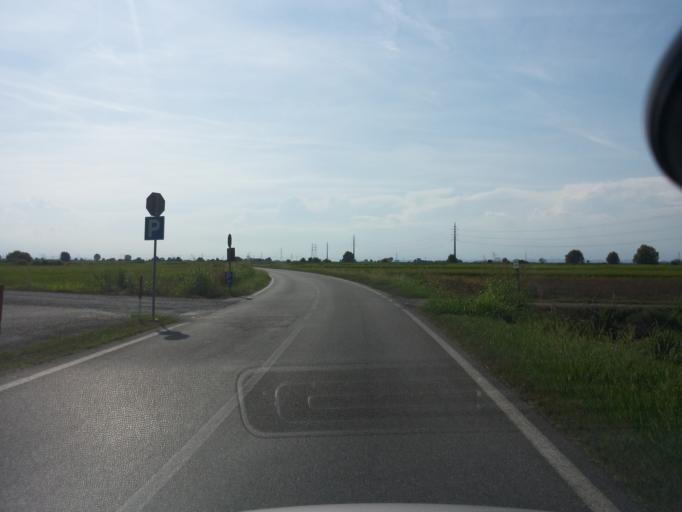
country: IT
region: Piedmont
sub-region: Provincia di Vercelli
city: Desana
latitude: 45.2750
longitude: 8.3593
